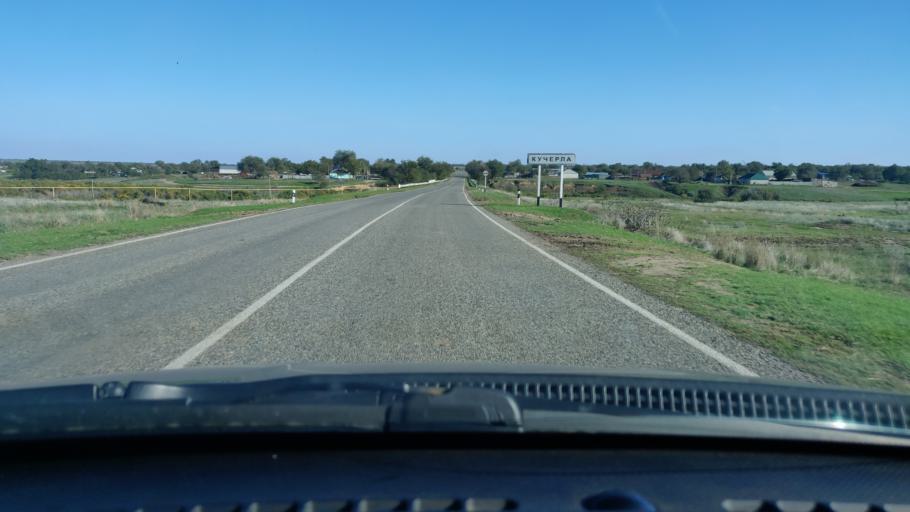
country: RU
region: Stavropol'skiy
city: Letnyaya Stavka
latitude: 45.3774
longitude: 43.6771
